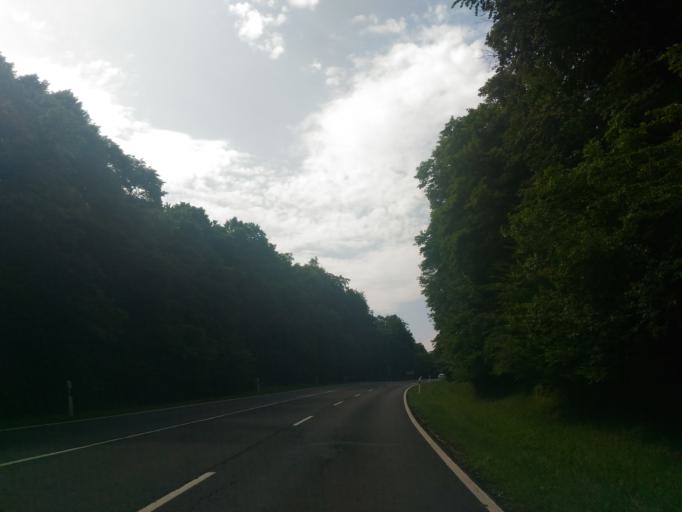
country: HU
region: Baranya
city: Komlo
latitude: 46.1403
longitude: 18.2505
